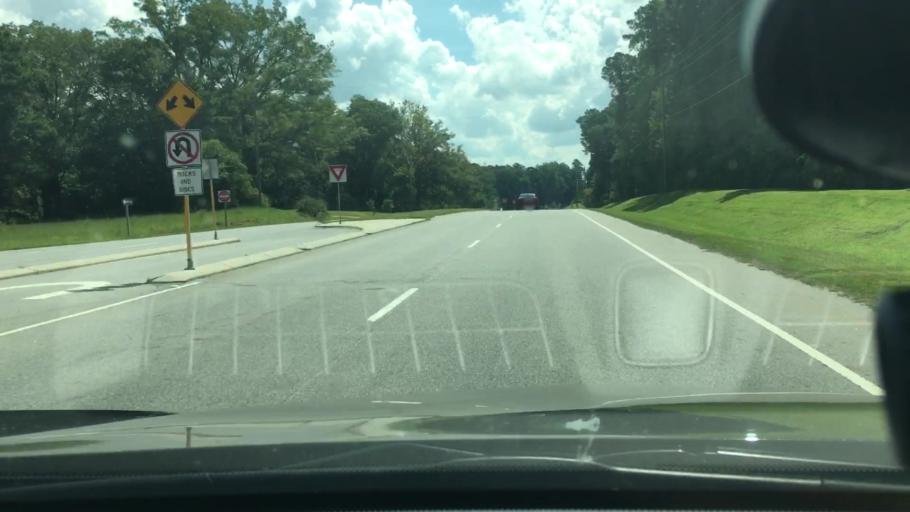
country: US
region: North Carolina
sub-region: Pitt County
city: Greenville
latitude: 35.6261
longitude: -77.4245
